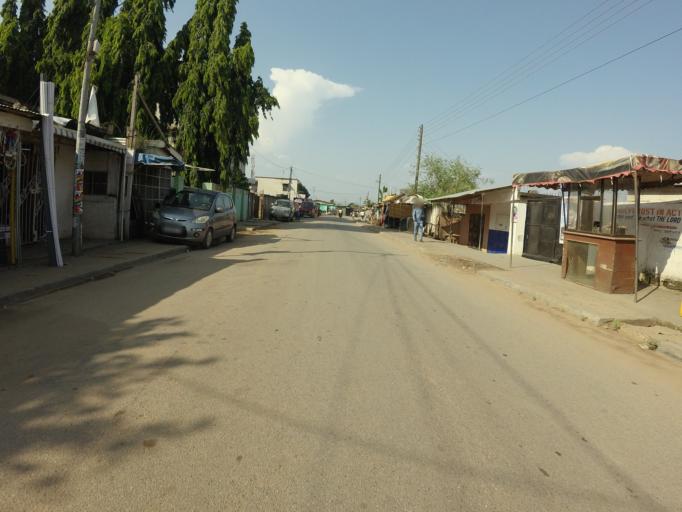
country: GH
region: Greater Accra
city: Dome
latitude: 5.6086
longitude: -0.2491
